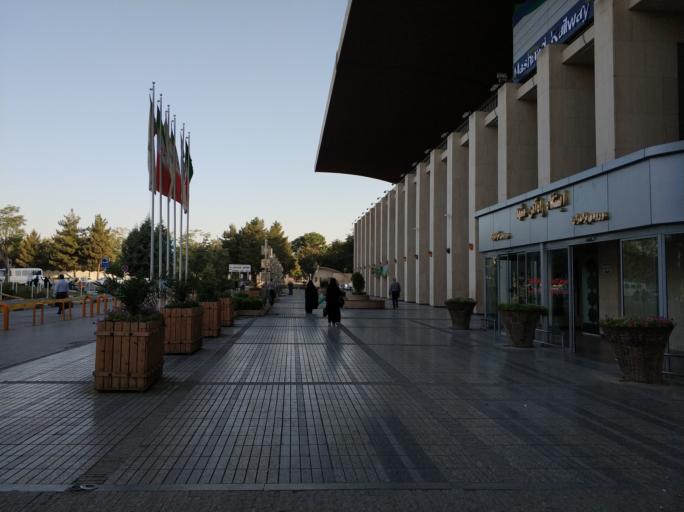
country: IR
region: Razavi Khorasan
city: Mashhad
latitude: 36.3043
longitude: 59.6234
